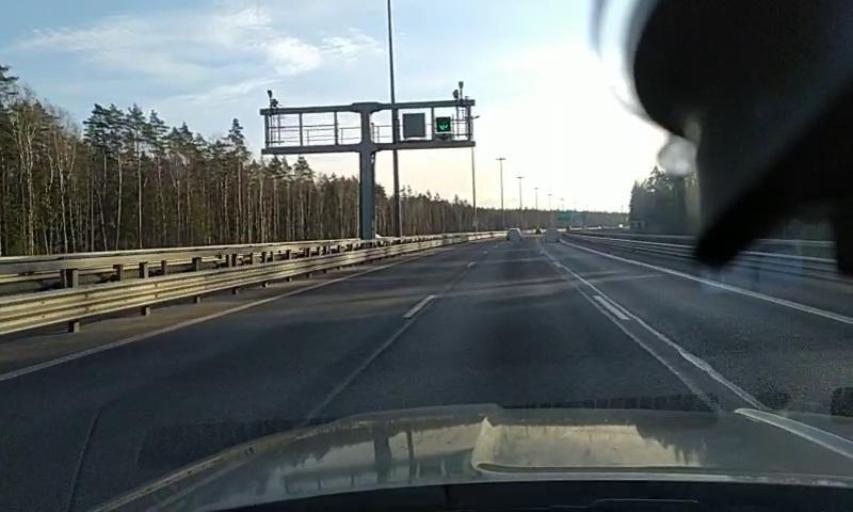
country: RU
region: St.-Petersburg
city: Pesochnyy
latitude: 60.0785
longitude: 30.1230
